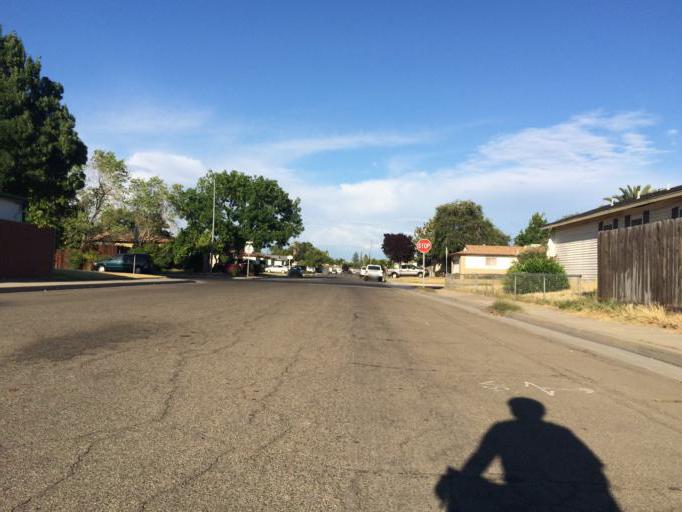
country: US
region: California
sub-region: Fresno County
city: Tarpey Village
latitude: 36.7982
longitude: -119.7142
